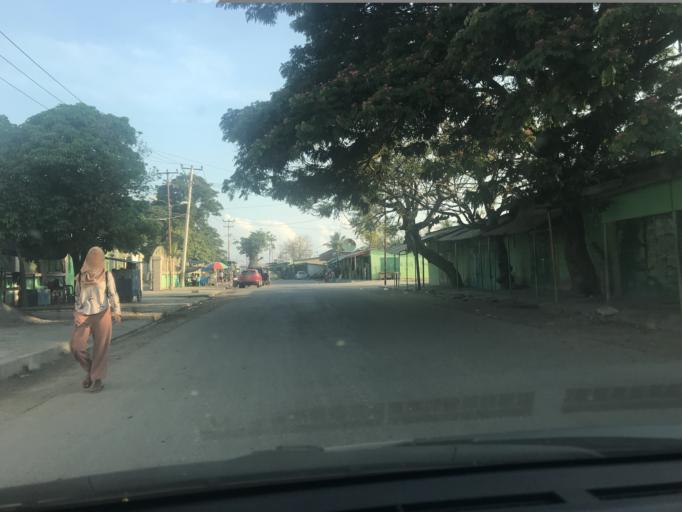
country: TL
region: Dili
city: Dili
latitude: -8.5503
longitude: 125.5607
